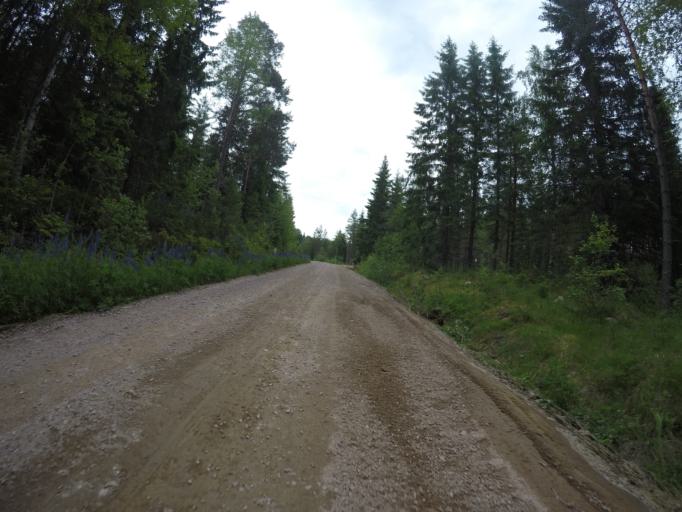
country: SE
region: Dalarna
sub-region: Ludvika Kommun
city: Abborrberget
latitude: 60.0961
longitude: 14.5451
